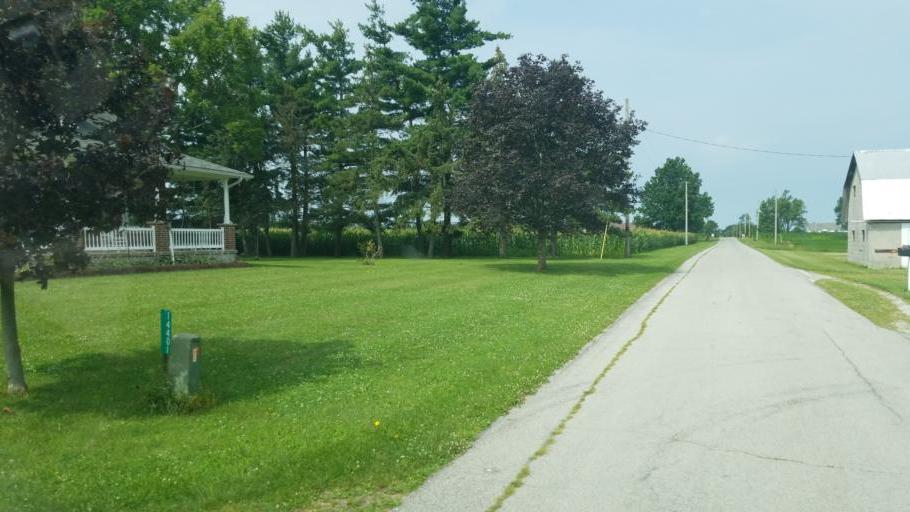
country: US
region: Ohio
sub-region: Wyandot County
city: Carey
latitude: 40.9271
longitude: -83.3890
